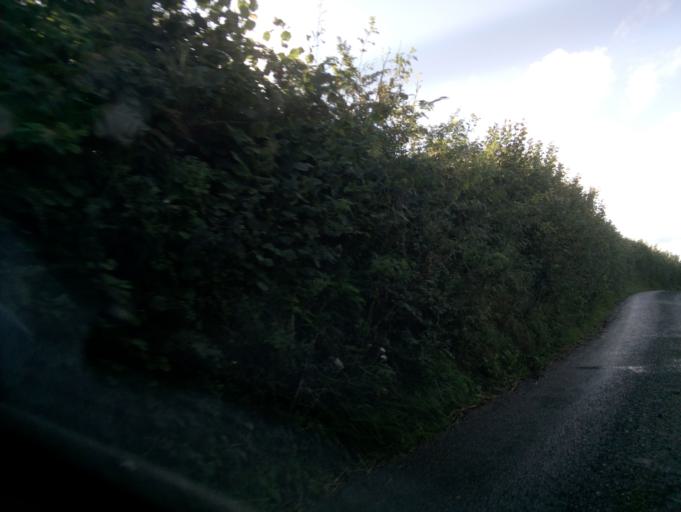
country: GB
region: England
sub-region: Devon
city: Dartmouth
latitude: 50.3433
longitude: -3.6099
